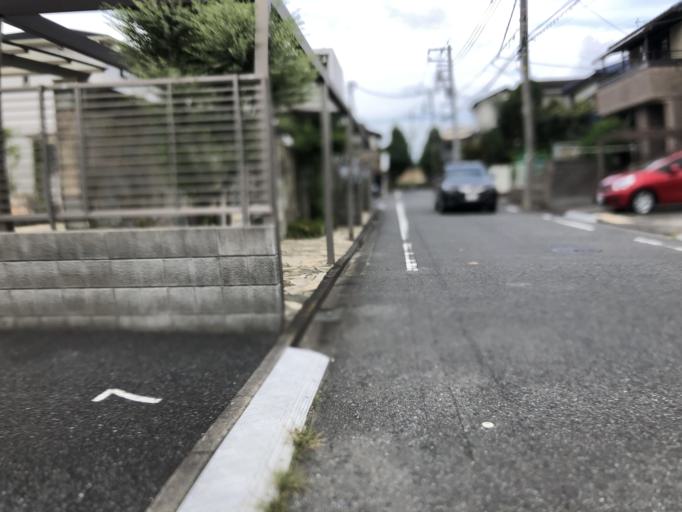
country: JP
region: Tokyo
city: Hachioji
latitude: 35.5871
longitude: 139.3463
